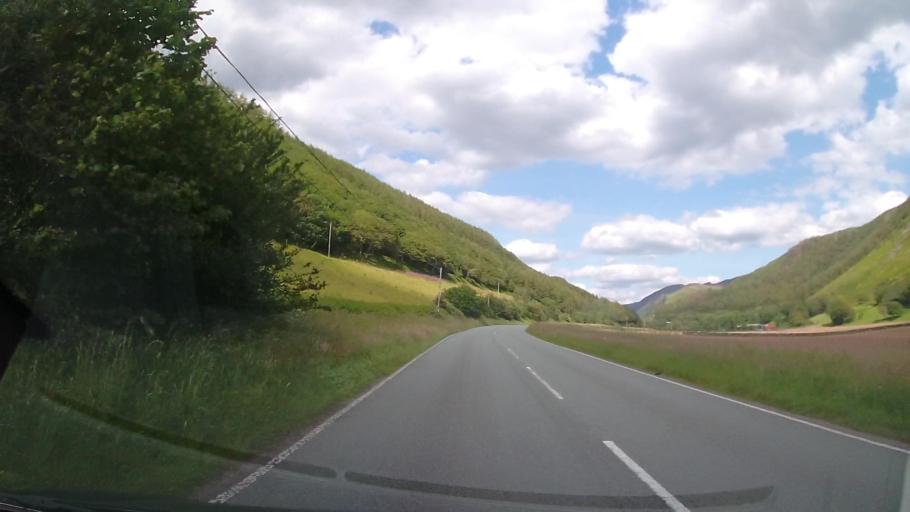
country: GB
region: Wales
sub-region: Gwynedd
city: Barmouth
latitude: 52.6347
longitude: -3.9787
